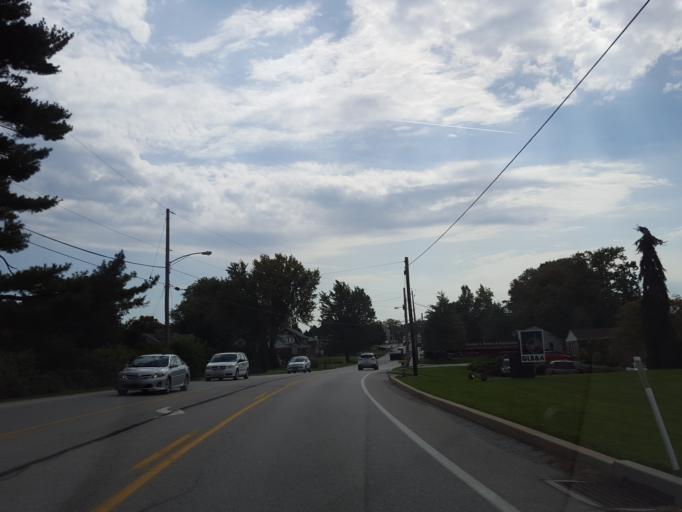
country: US
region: Pennsylvania
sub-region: York County
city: Spry
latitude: 39.9253
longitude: -76.6856
